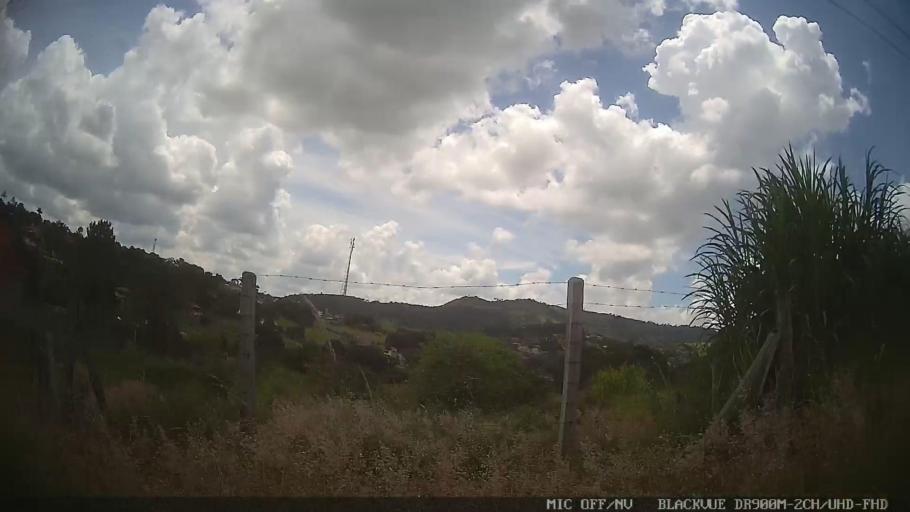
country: BR
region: Sao Paulo
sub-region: Braganca Paulista
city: Braganca Paulista
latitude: -23.0341
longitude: -46.5343
